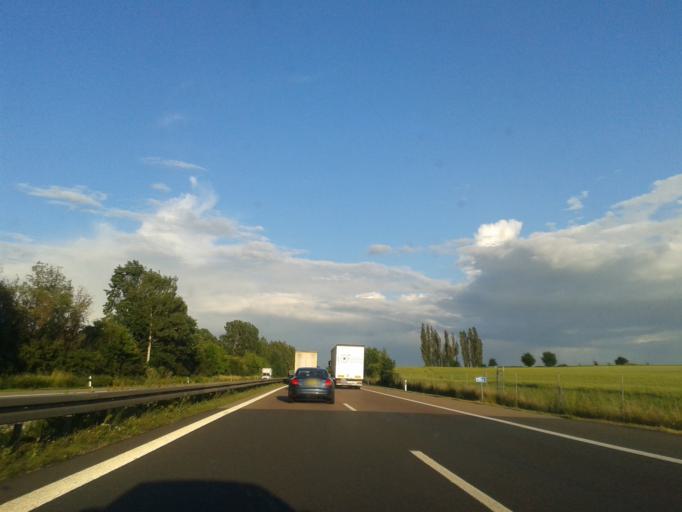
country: DE
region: Saxony
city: Ostrau
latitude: 51.2328
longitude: 12.8897
